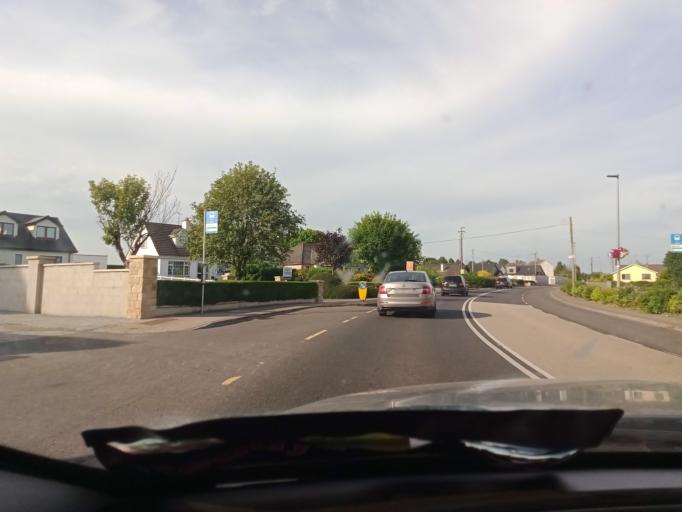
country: IE
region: Ulster
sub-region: An Cabhan
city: Cavan
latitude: 53.9338
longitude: -7.4075
